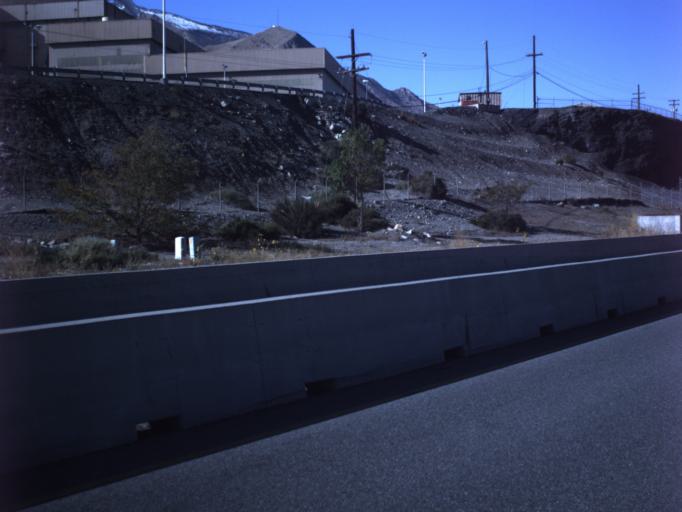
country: US
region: Utah
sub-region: Salt Lake County
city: Magna
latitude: 40.7273
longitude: -112.1932
